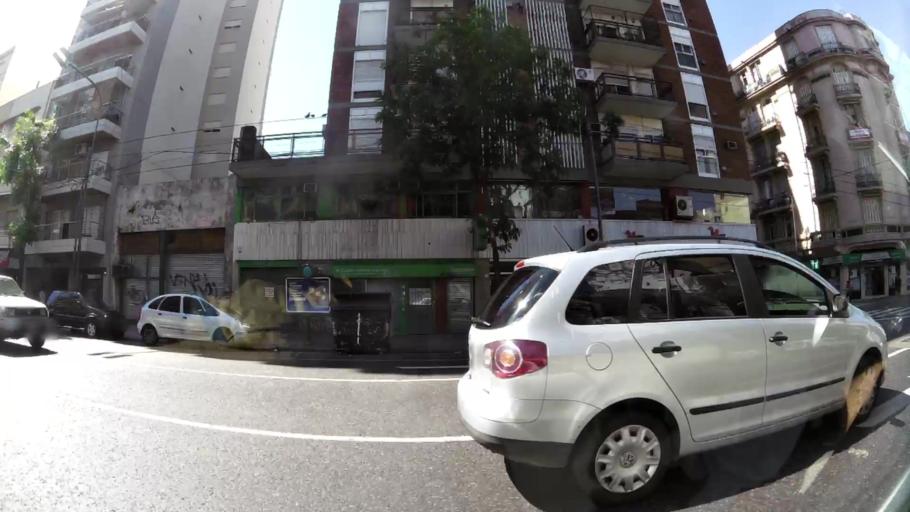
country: AR
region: Buenos Aires F.D.
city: Buenos Aires
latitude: -34.6230
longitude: -58.3956
